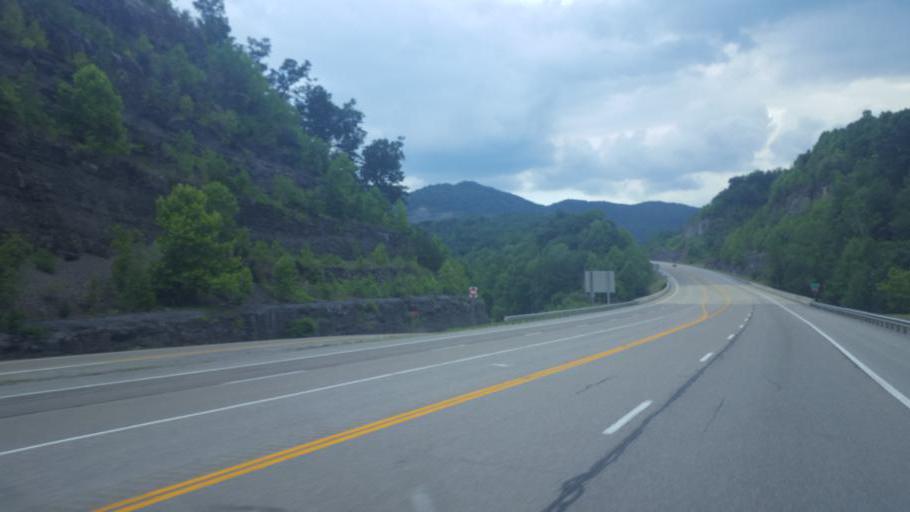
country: US
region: Kentucky
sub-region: Letcher County
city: Jenkins
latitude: 37.1776
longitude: -82.6408
